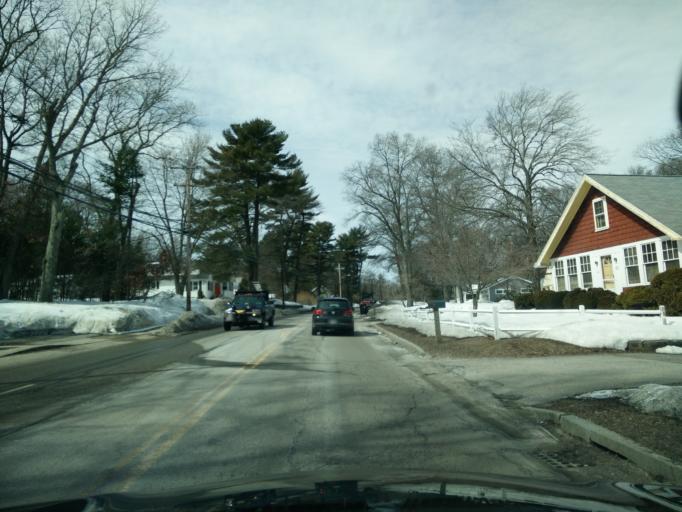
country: US
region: Massachusetts
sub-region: Norfolk County
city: Walpole
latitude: 42.1424
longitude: -71.2226
